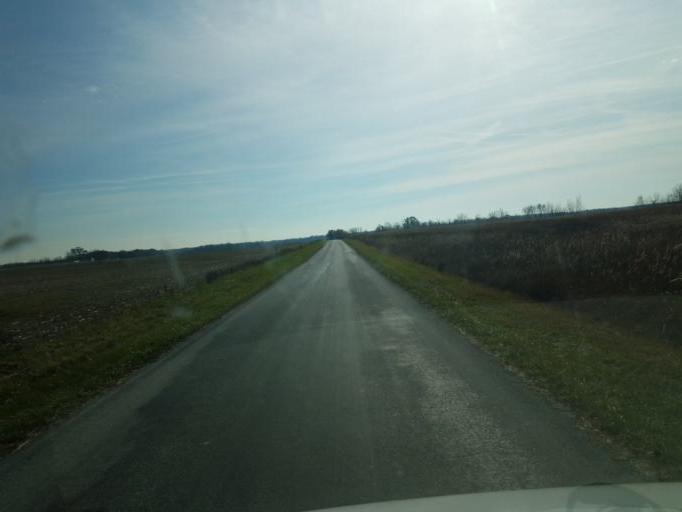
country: US
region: Ohio
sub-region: Hardin County
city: Kenton
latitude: 40.6277
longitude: -83.4386
